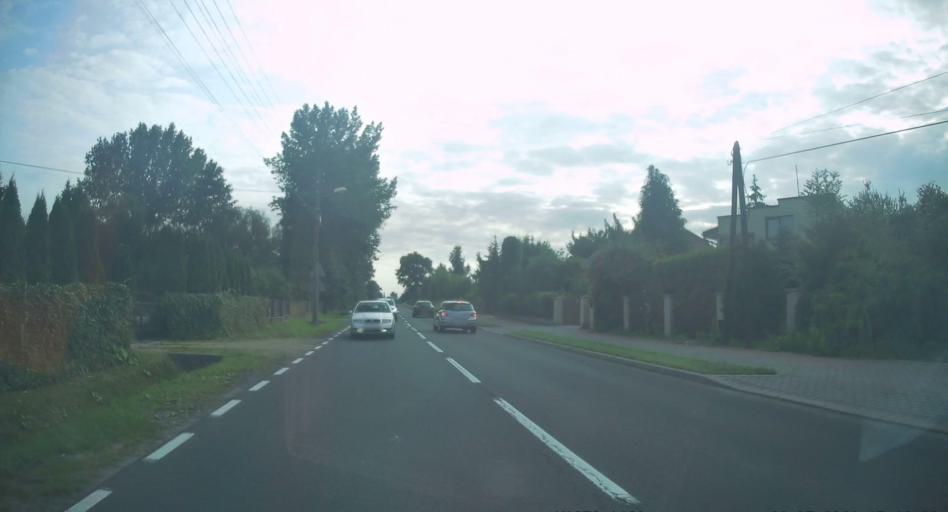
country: PL
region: Silesian Voivodeship
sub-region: Powiat czestochowski
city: Klomnice
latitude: 50.9275
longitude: 19.3742
